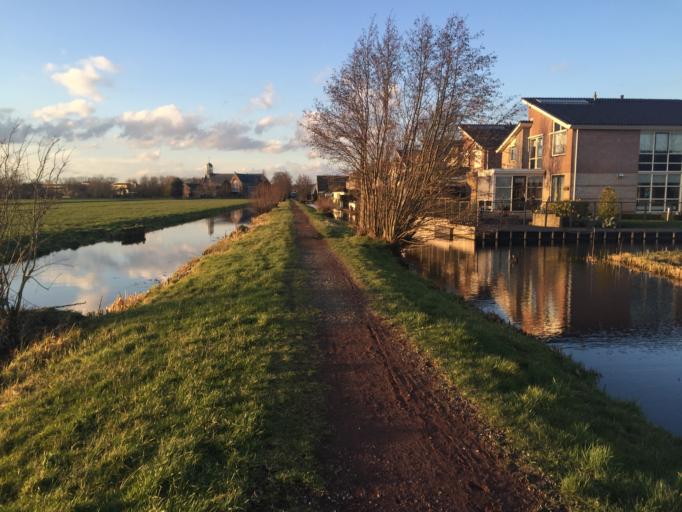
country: NL
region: Utrecht
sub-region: Gemeente Oudewater
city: Oudewater
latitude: 52.0577
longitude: 4.8221
